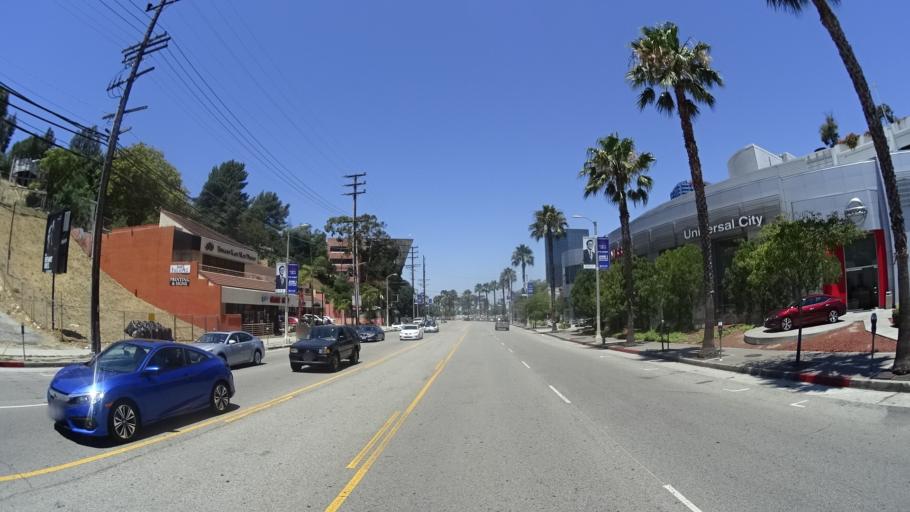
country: US
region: California
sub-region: Los Angeles County
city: Universal City
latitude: 34.1331
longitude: -118.3564
